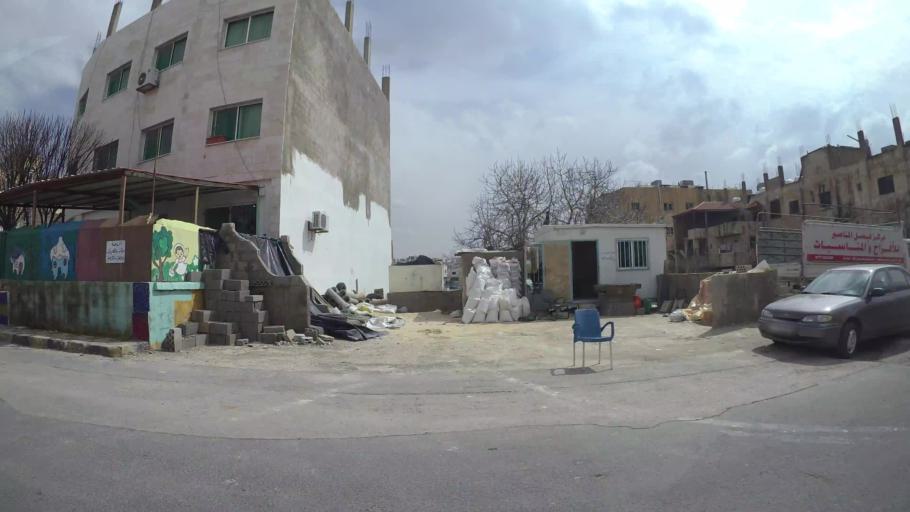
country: JO
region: Amman
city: Umm as Summaq
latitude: 31.8987
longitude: 35.8394
